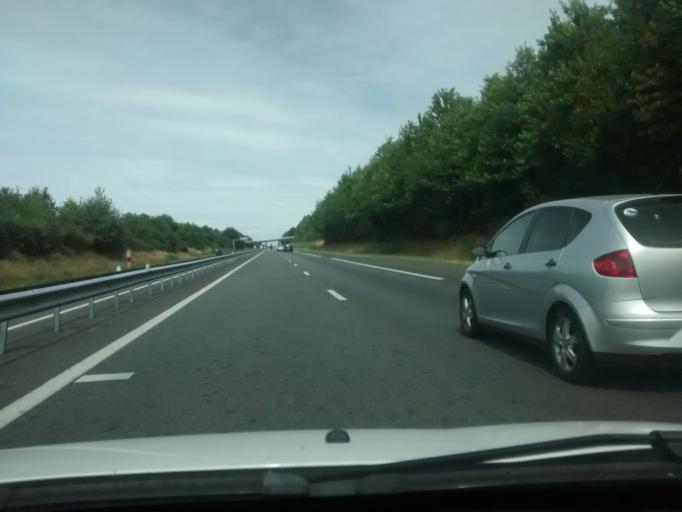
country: FR
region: Brittany
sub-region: Departement d'Ille-et-Vilaine
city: Saint-Etienne-en-Cogles
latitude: 48.4448
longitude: -1.3244
